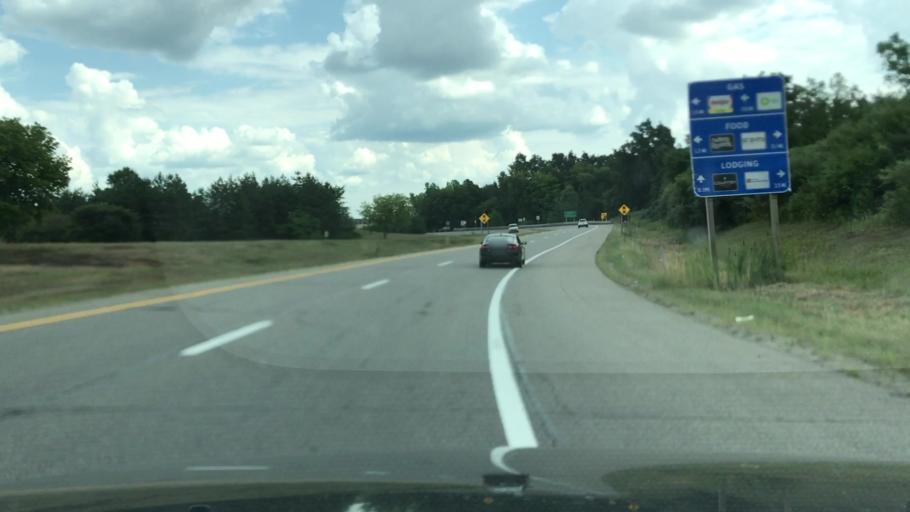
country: US
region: Michigan
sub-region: Kent County
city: East Grand Rapids
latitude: 42.9731
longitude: -85.5945
